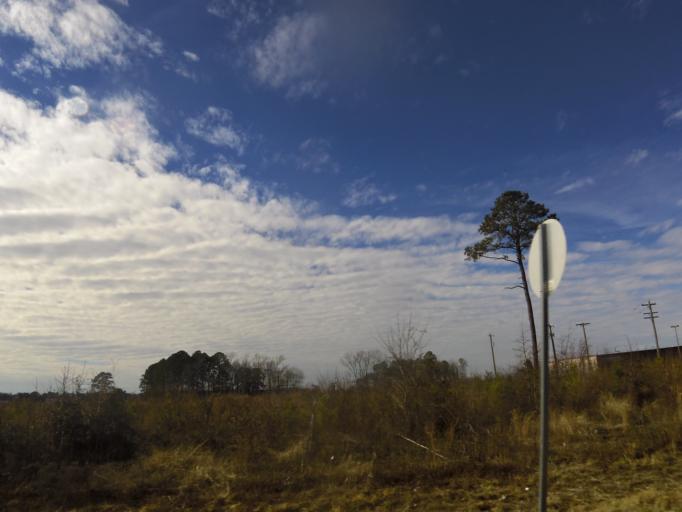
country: US
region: Virginia
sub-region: City of Franklin
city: Franklin
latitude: 36.6946
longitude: -76.8944
